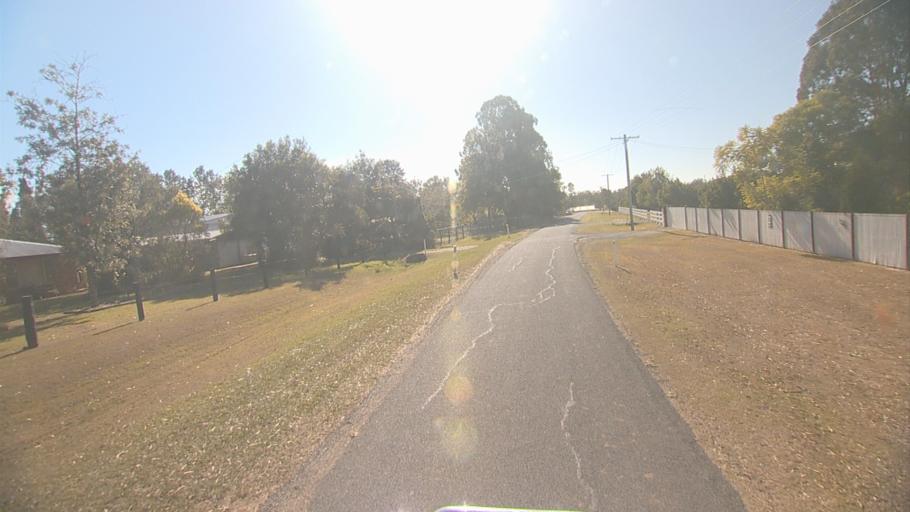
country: AU
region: Queensland
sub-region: Logan
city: Cedar Vale
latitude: -27.8450
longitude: 152.9882
